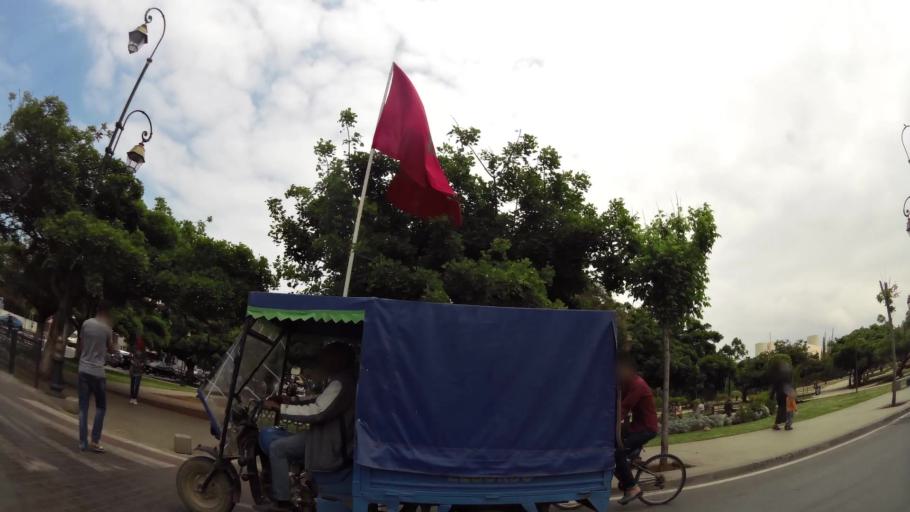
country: MA
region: Rabat-Sale-Zemmour-Zaer
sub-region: Skhirate-Temara
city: Temara
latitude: 33.9765
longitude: -6.8866
